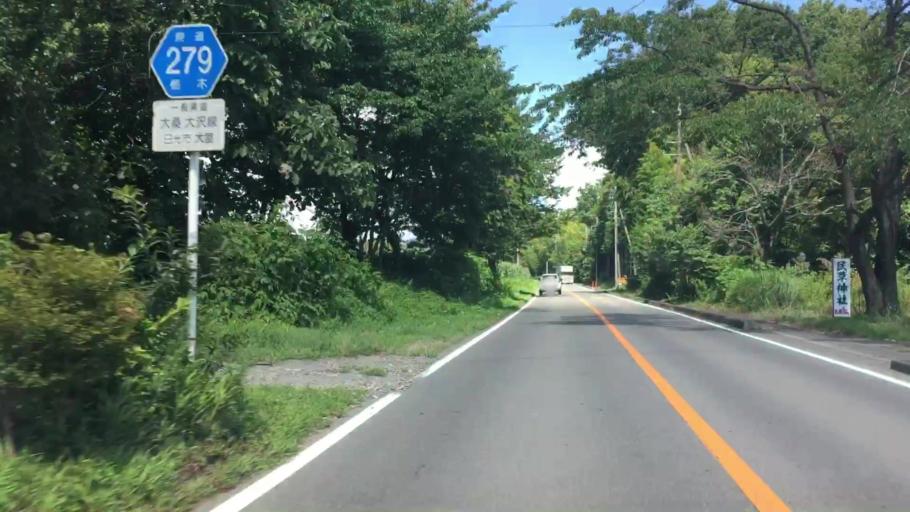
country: JP
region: Tochigi
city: Imaichi
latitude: 36.7165
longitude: 139.7508
